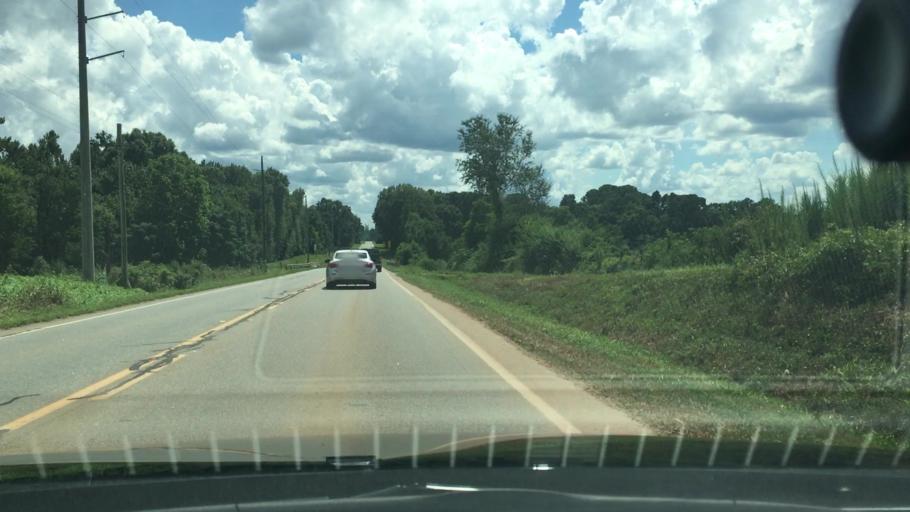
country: US
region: Georgia
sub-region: Putnam County
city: Eatonton
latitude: 33.3457
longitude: -83.3590
